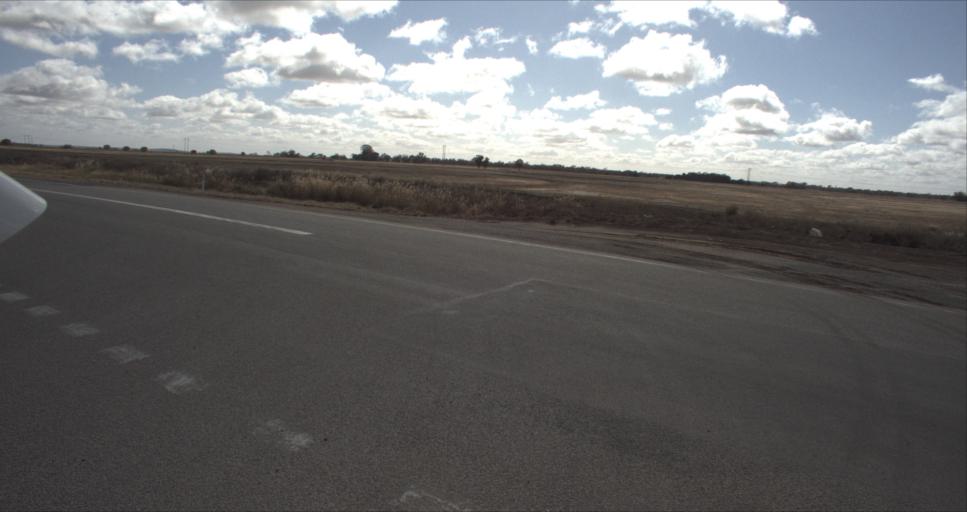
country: AU
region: New South Wales
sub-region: Murrumbidgee Shire
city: Darlington Point
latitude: -34.5167
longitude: 146.1854
